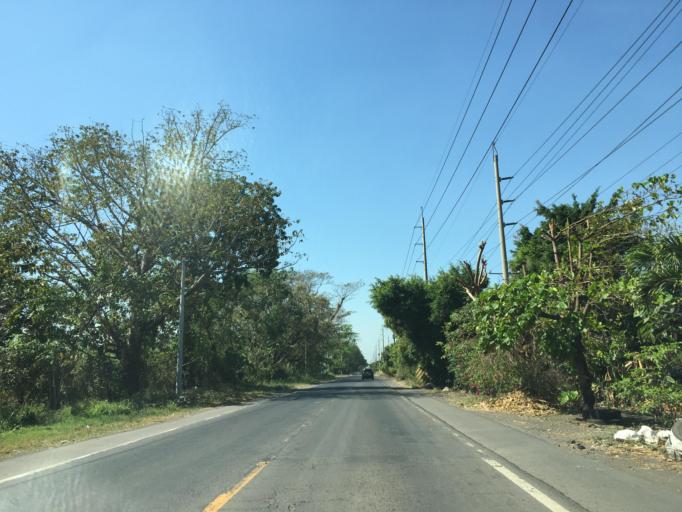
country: GT
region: Escuintla
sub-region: Municipio de Masagua
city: Masagua
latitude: 14.2263
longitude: -90.8274
